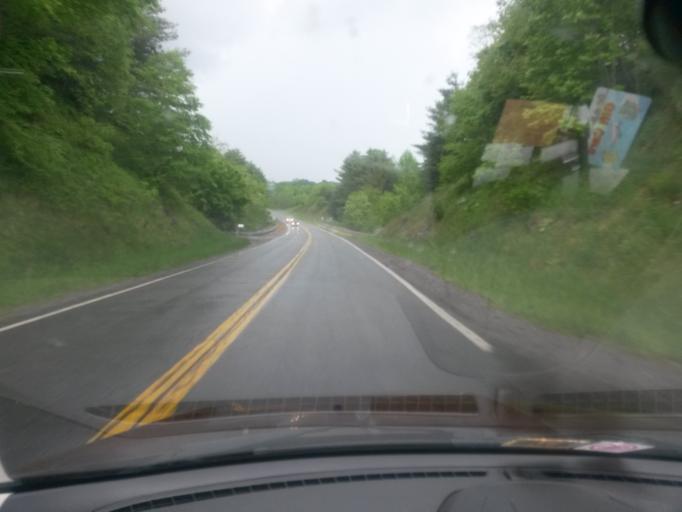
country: US
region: Virginia
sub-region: Floyd County
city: Floyd
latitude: 36.9644
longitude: -80.3730
